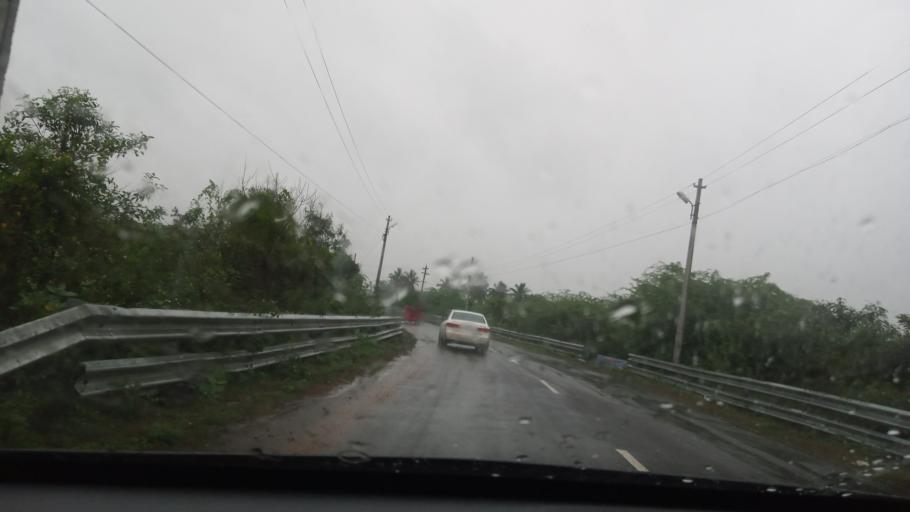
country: IN
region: Tamil Nadu
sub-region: Tiruvannamalai
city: Cheyyar
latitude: 12.6517
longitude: 79.5389
